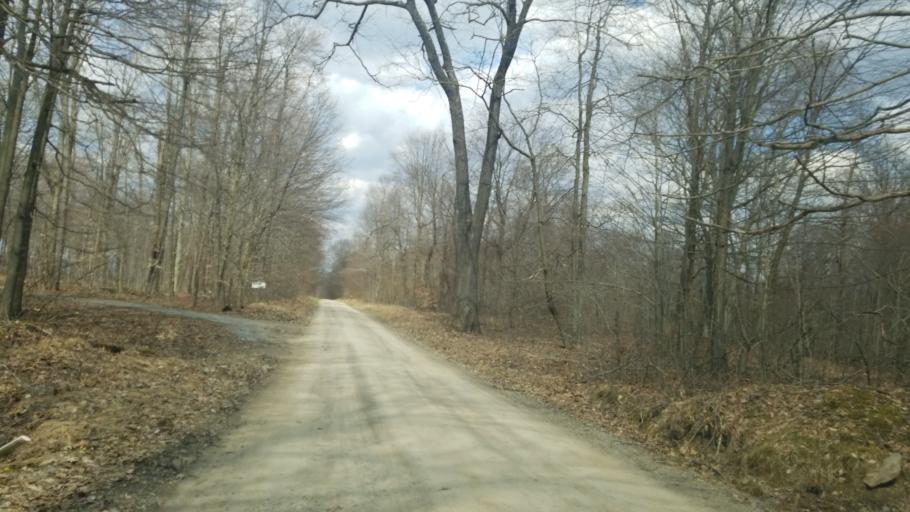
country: US
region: Pennsylvania
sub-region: Clearfield County
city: Clearfield
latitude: 41.1419
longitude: -78.5196
